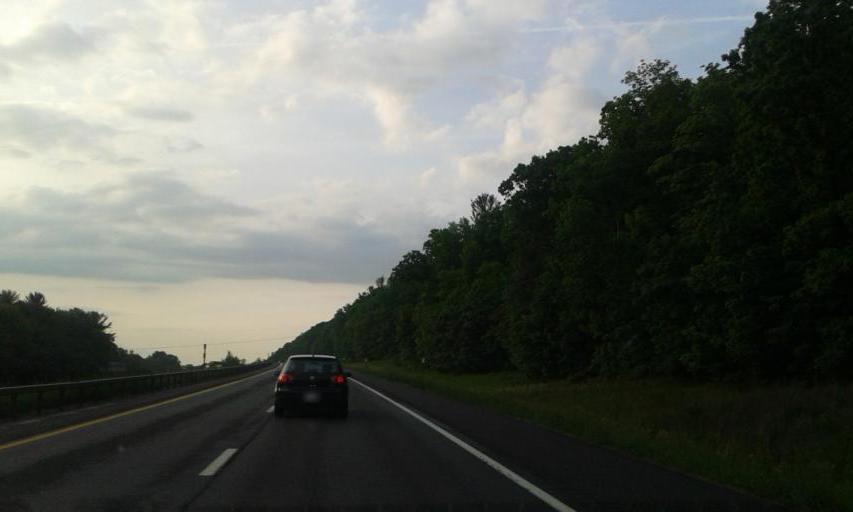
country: US
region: New York
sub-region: Broome County
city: Chenango Bridge
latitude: 42.1736
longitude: -75.8973
